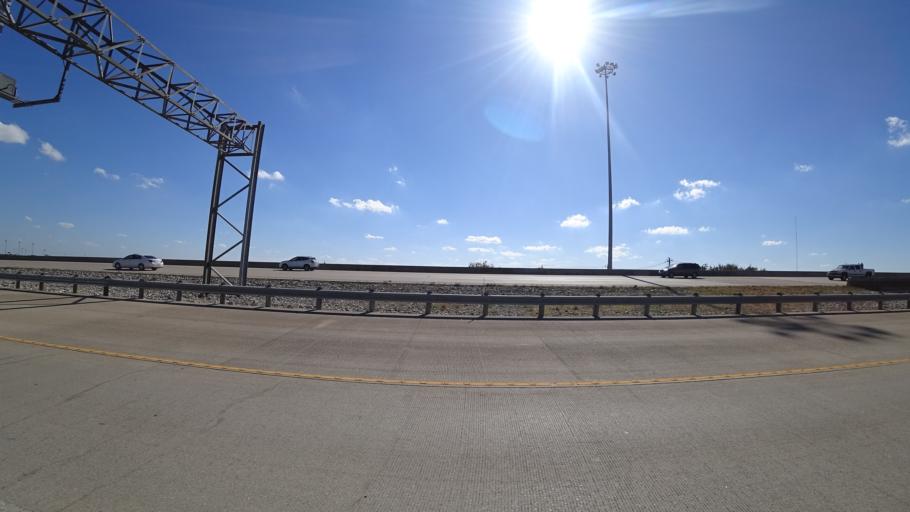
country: US
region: Texas
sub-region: Travis County
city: Rollingwood
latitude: 30.2333
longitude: -97.8173
